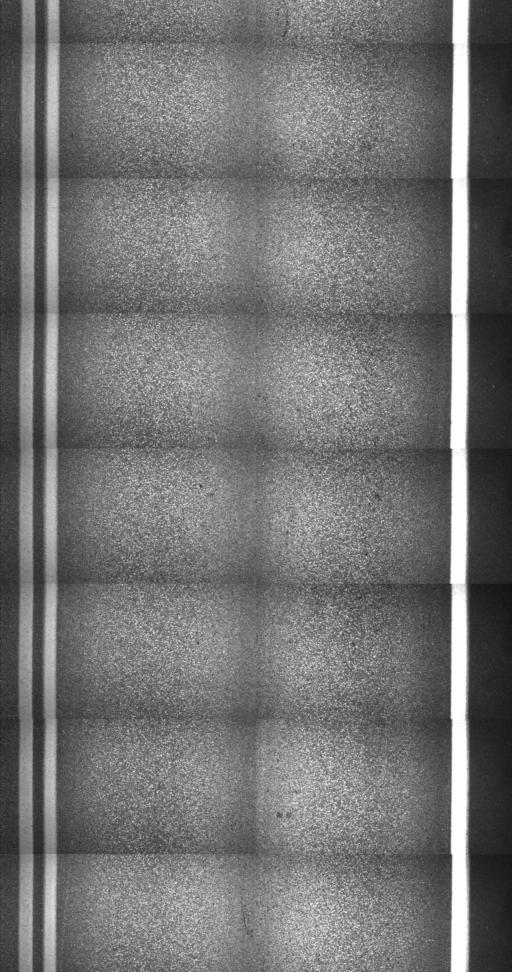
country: US
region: Vermont
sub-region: Windham County
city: Dover
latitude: 42.8058
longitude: -72.8345
